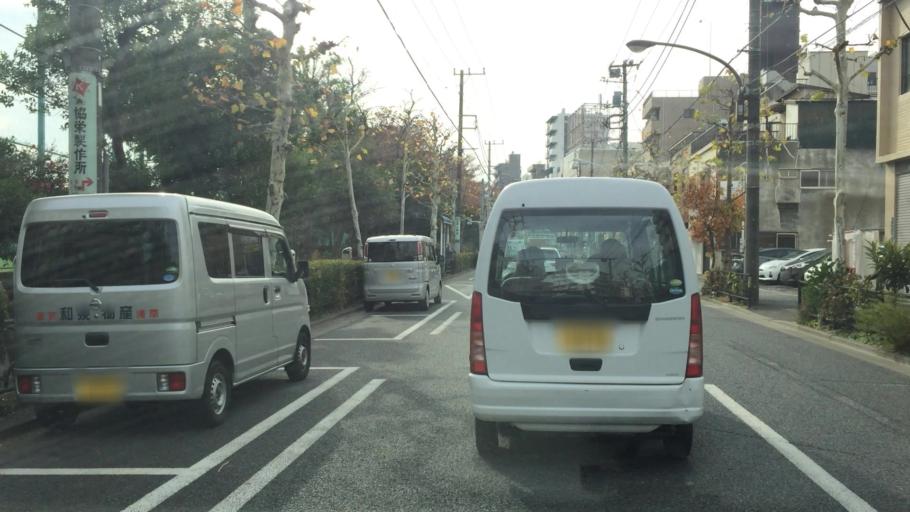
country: JP
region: Tokyo
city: Urayasu
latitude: 35.7205
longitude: 139.8064
